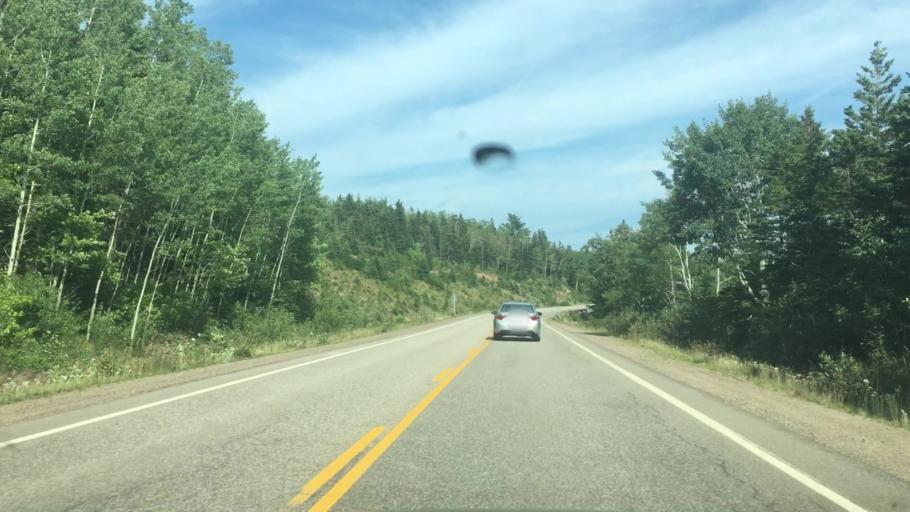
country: CA
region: Nova Scotia
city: Sydney Mines
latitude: 46.7136
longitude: -60.3586
